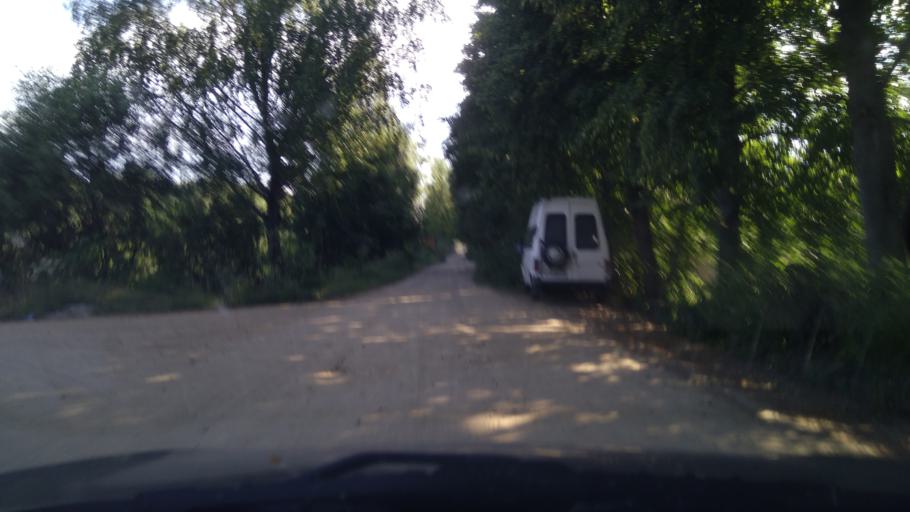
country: BY
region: Brest
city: Byelaazyorsk
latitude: 52.4472
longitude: 25.1788
